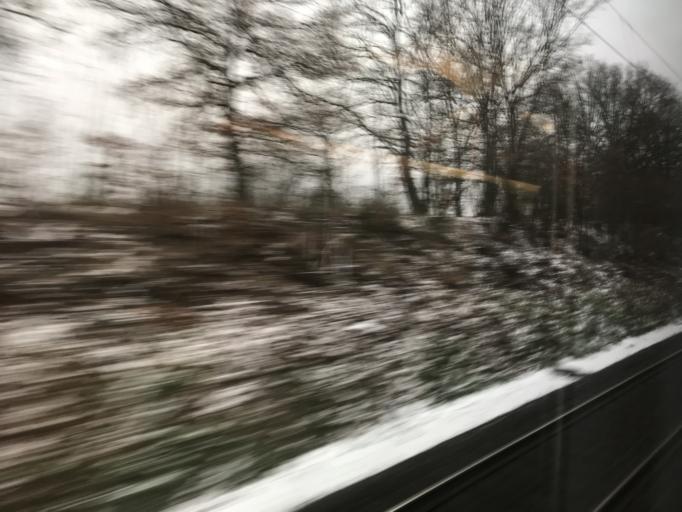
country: DE
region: Hesse
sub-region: Regierungsbezirk Kassel
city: Neuhof
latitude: 50.4652
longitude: 9.6377
